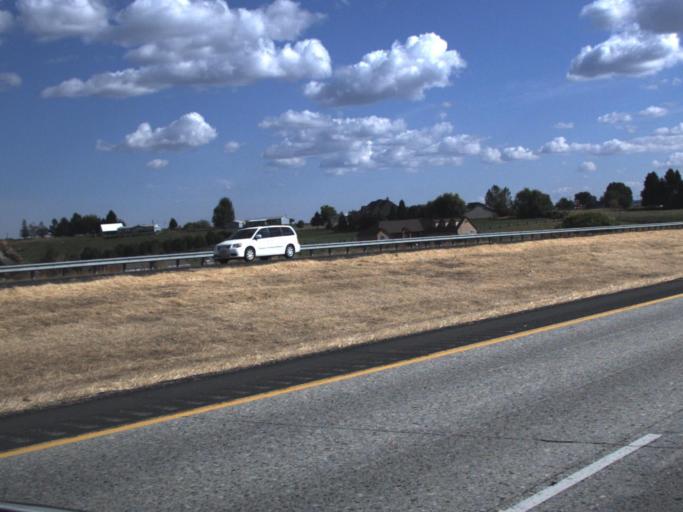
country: US
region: Washington
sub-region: Yakima County
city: Granger
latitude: 46.3733
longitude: -120.2172
